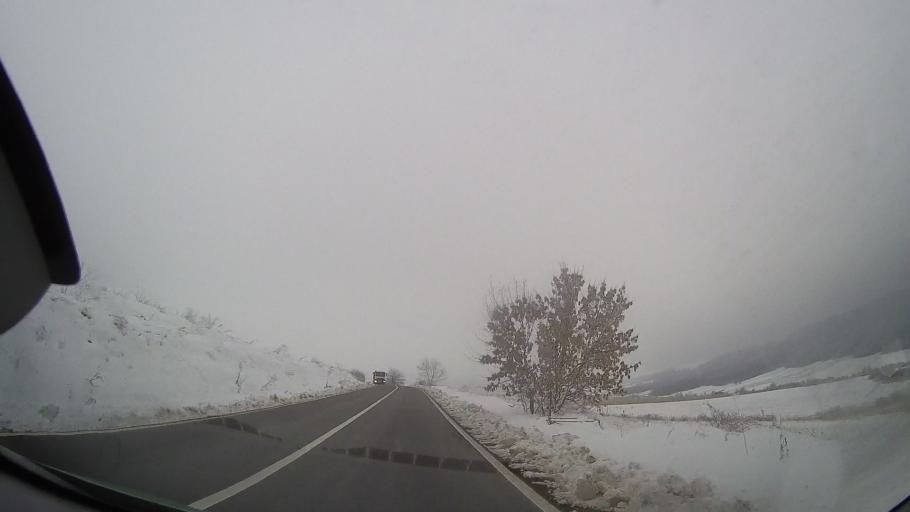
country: RO
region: Neamt
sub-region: Comuna Poenari
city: Poienari
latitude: 46.8721
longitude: 27.1417
